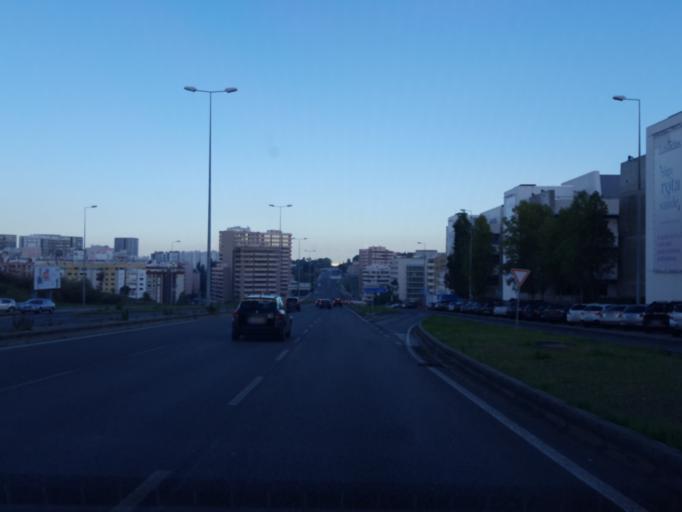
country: PT
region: Lisbon
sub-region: Odivelas
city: Pontinha
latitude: 38.7498
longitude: -9.1775
